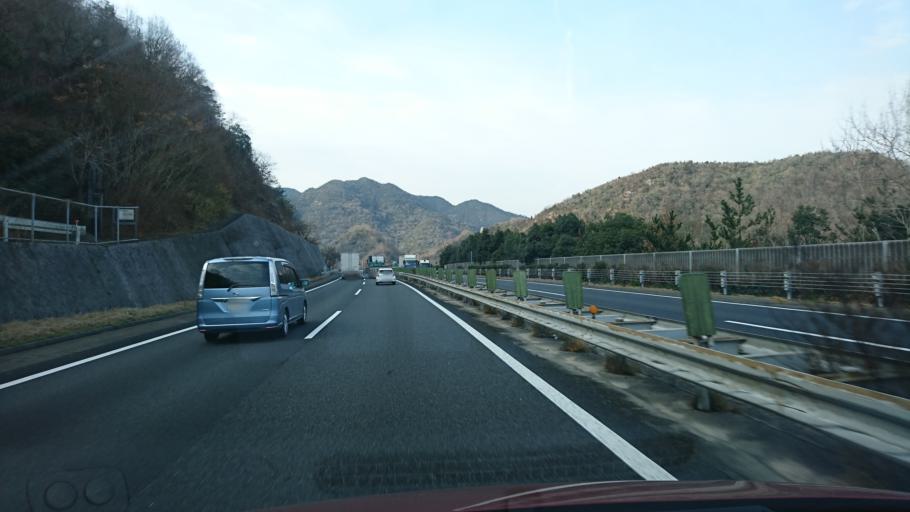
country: JP
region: Hyogo
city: Kariya
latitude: 34.7907
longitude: 134.1707
